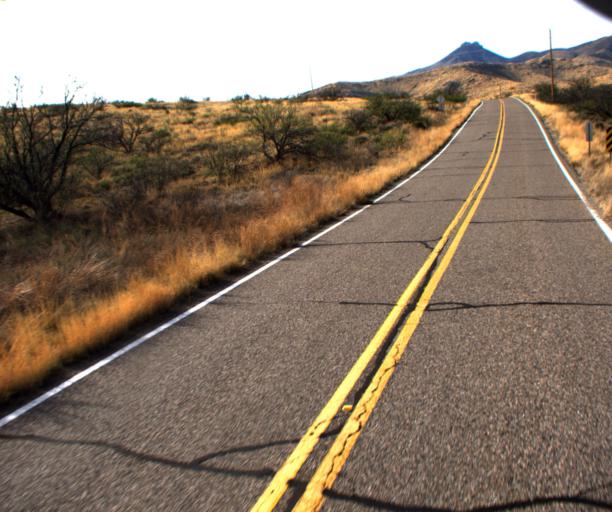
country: US
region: Arizona
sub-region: Cochise County
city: Willcox
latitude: 32.1572
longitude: -109.5654
